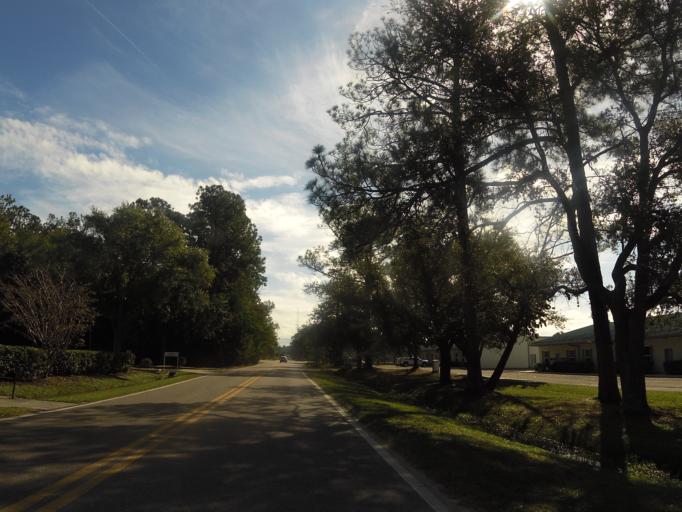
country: US
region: Florida
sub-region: Duval County
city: Jacksonville
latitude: 30.2664
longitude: -81.6134
